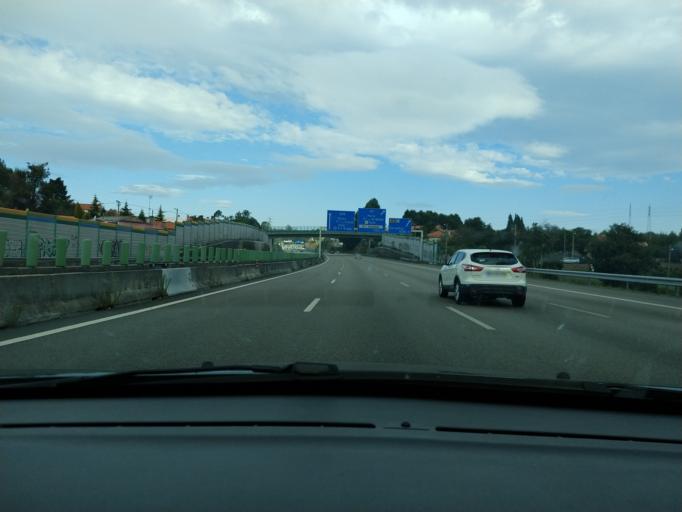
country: PT
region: Porto
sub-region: Vila Nova de Gaia
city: Perozinho
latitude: 41.0589
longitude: -8.5783
